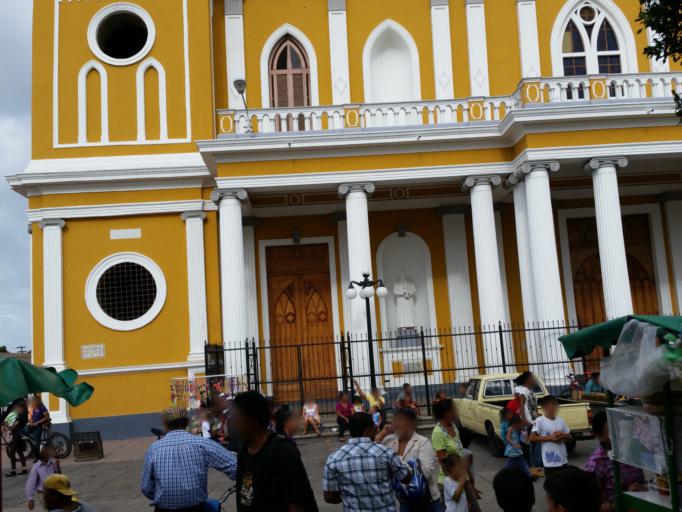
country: NI
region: Granada
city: Granada
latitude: 11.9299
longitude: -85.9538
